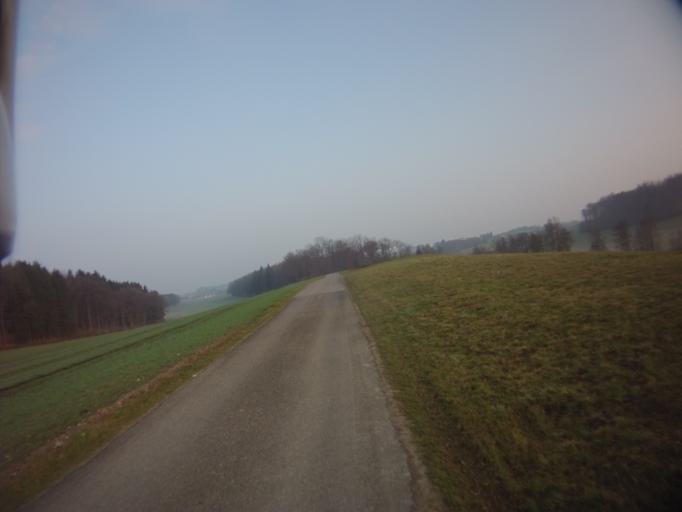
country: CH
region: Zurich
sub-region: Bezirk Affoltern
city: Knonau
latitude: 47.2247
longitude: 8.4463
